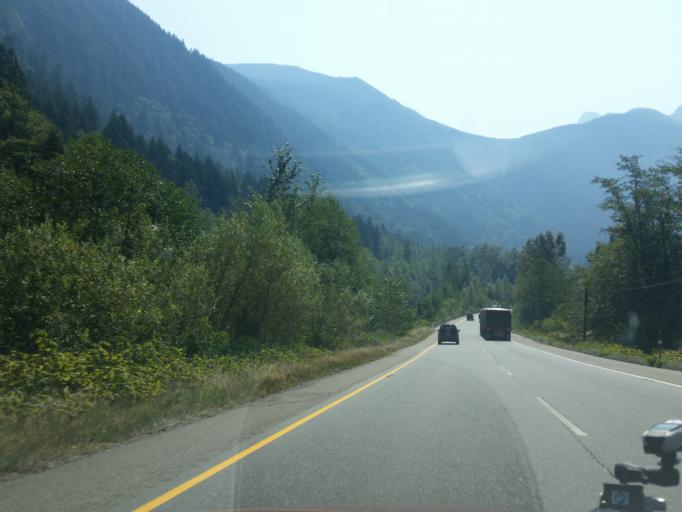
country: CA
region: British Columbia
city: Agassiz
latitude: 49.2508
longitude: -121.6802
